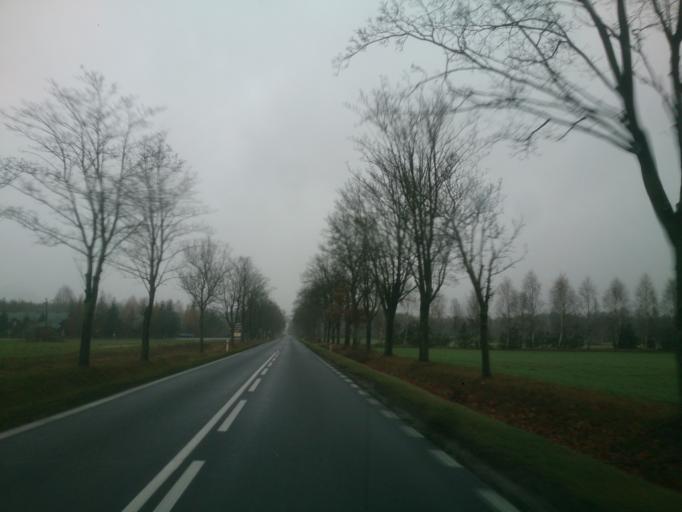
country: PL
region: Masovian Voivodeship
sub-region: Powiat sierpecki
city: Sierpc
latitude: 52.8978
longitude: 19.6476
